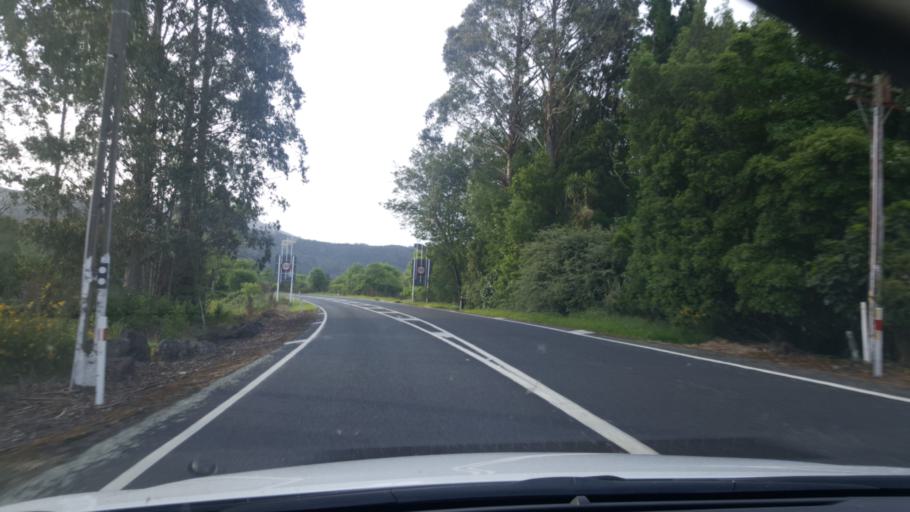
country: NZ
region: Waikato
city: Turangi
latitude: -38.9606
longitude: 175.7638
